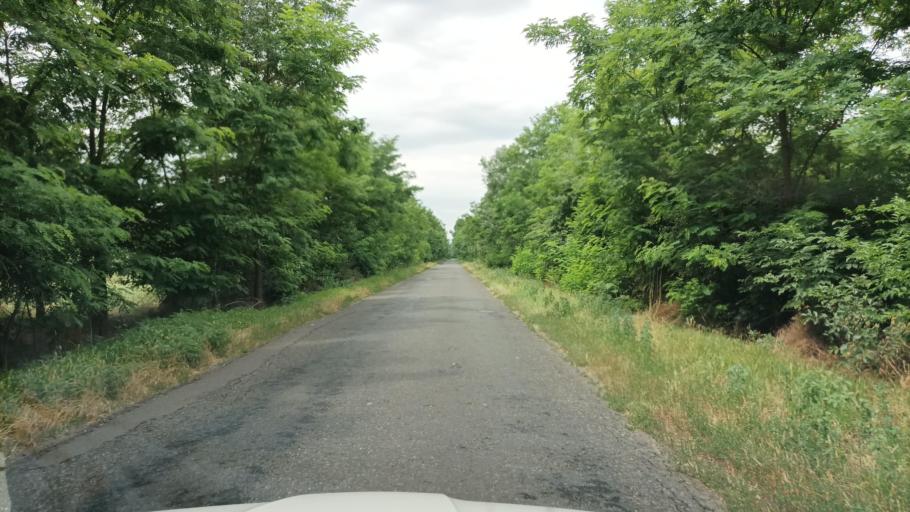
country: HU
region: Pest
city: Orkeny
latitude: 47.0476
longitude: 19.3365
